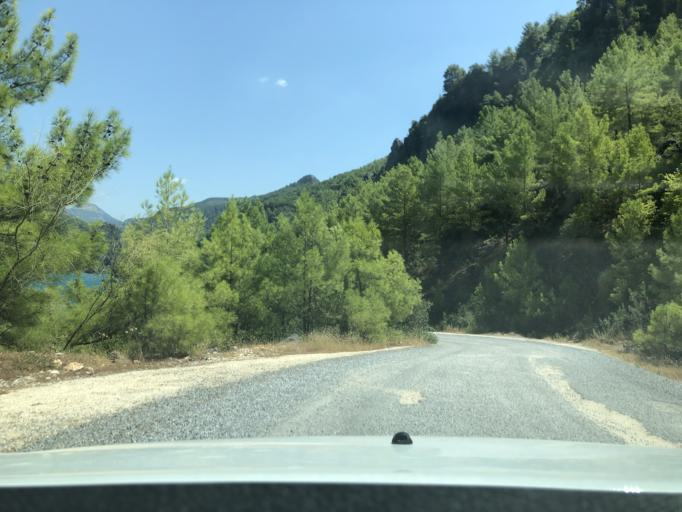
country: TR
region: Antalya
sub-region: Manavgat
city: Manavgat
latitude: 36.9089
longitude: 31.5523
